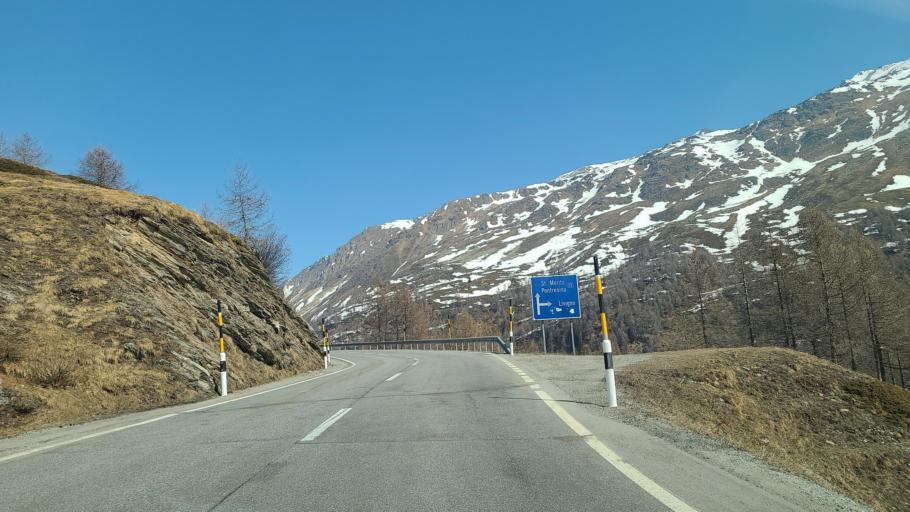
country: CH
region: Grisons
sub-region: Bernina District
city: Poschiavo
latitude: 46.4100
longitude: 10.0517
